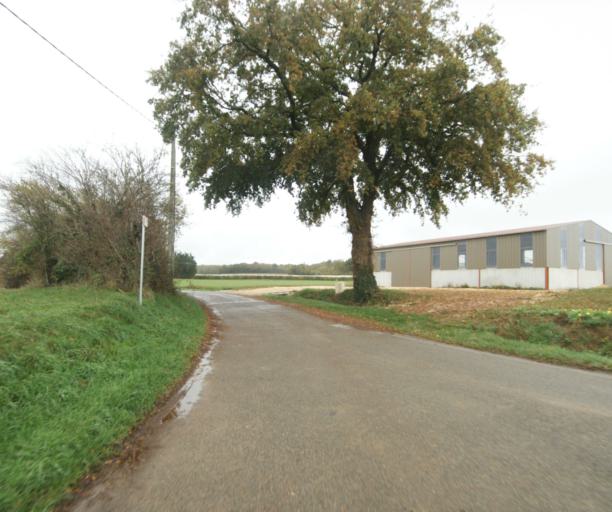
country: FR
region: Rhone-Alpes
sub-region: Departement de l'Ain
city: Pont-de-Vaux
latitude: 46.4788
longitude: 4.8598
